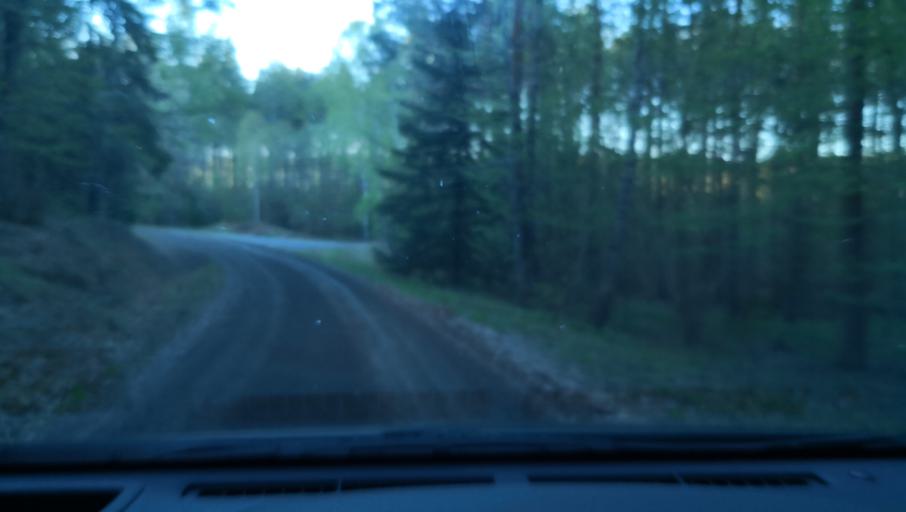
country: SE
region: OErebro
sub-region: Askersunds Kommun
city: Asbro
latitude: 58.8748
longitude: 15.1451
